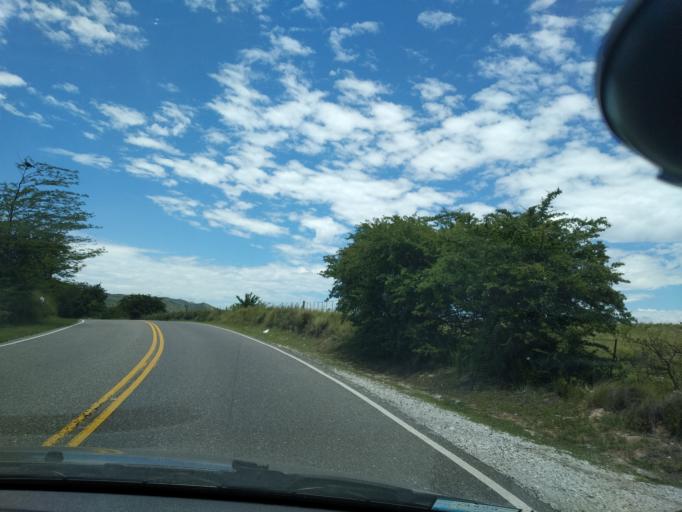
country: AR
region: Cordoba
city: Cuesta Blanca
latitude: -31.5993
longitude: -64.5635
